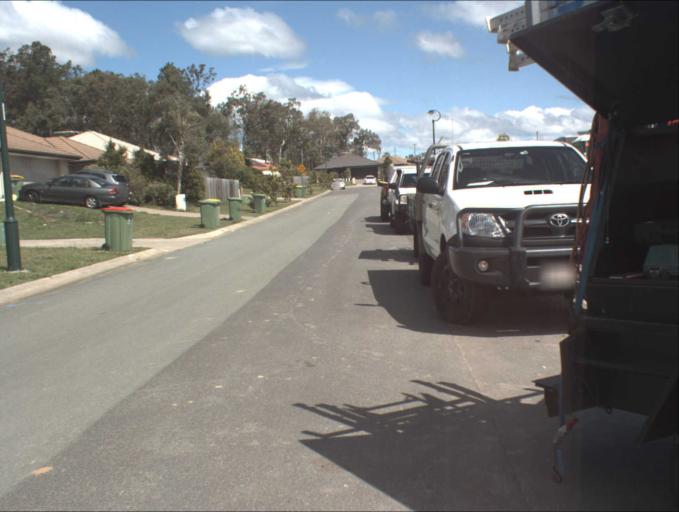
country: AU
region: Queensland
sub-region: Logan
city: Park Ridge South
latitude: -27.6717
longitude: 153.0289
